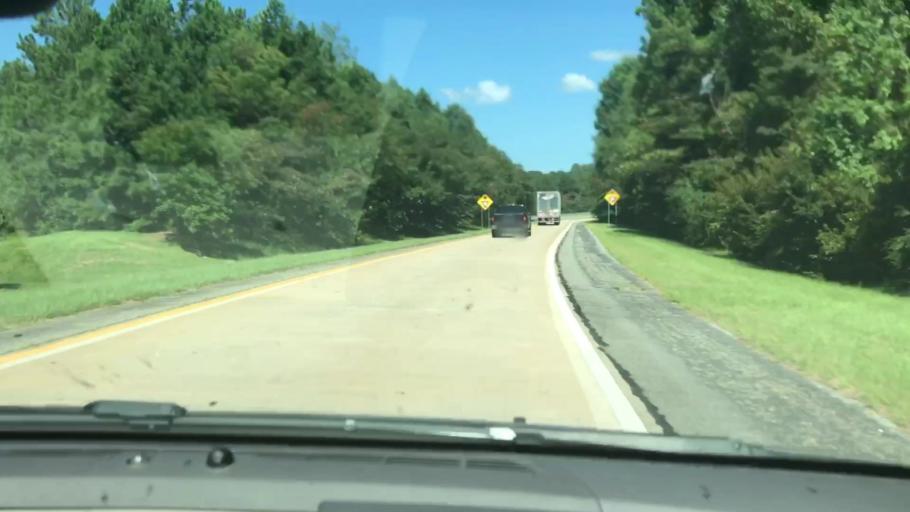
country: US
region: Alabama
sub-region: Russell County
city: Phenix City
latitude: 32.5476
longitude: -84.9591
